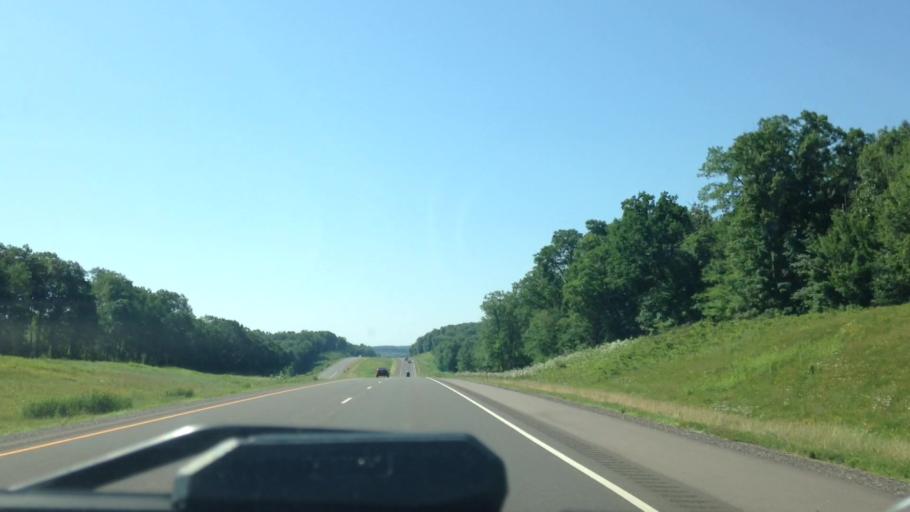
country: US
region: Wisconsin
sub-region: Washburn County
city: Spooner
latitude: 46.0028
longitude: -91.8333
